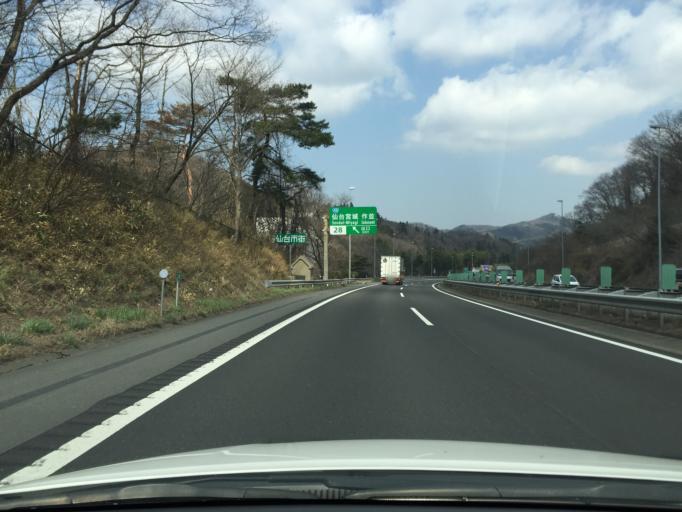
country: JP
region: Miyagi
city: Sendai
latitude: 38.2540
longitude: 140.8120
